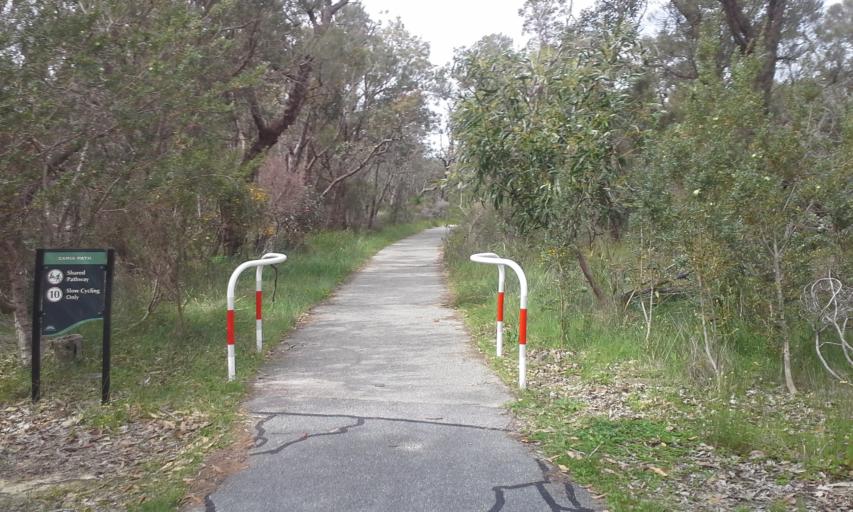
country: AU
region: Western Australia
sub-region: Subiaco
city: Crawley
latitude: -31.9692
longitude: 115.8260
